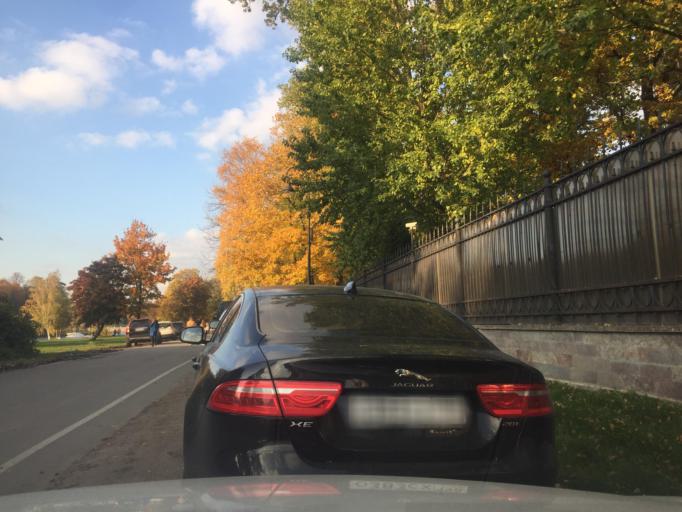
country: RU
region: St.-Petersburg
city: Novaya Derevnya
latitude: 59.9776
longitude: 30.2750
